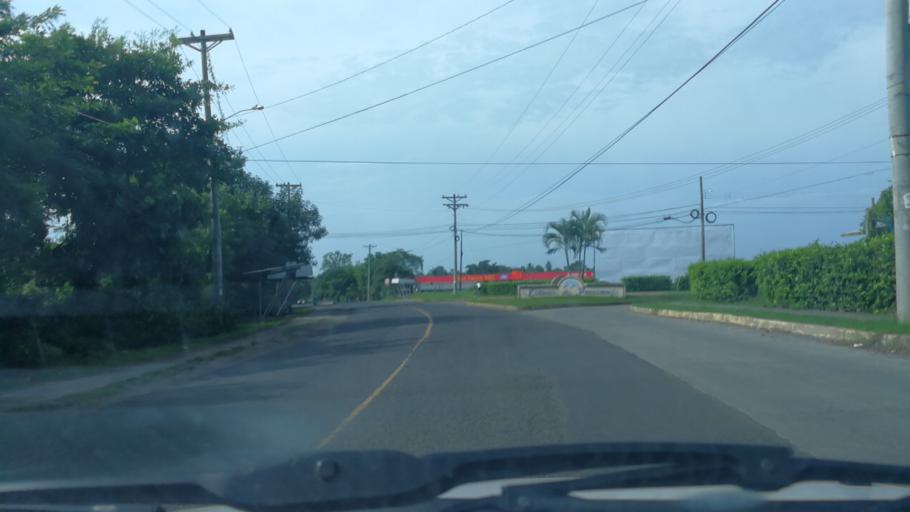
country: PA
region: Panama
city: Pacora
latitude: 9.0896
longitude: -79.2884
